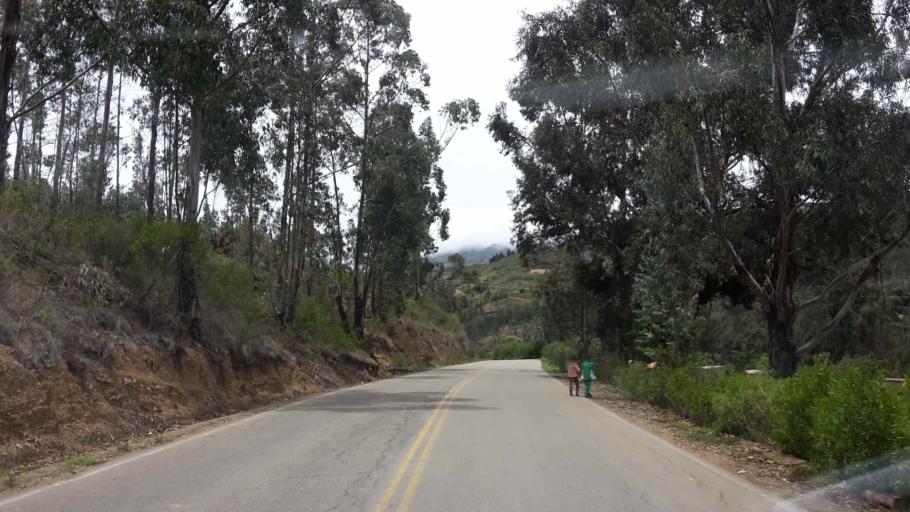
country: BO
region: Cochabamba
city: Totora
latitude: -17.6754
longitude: -65.2190
